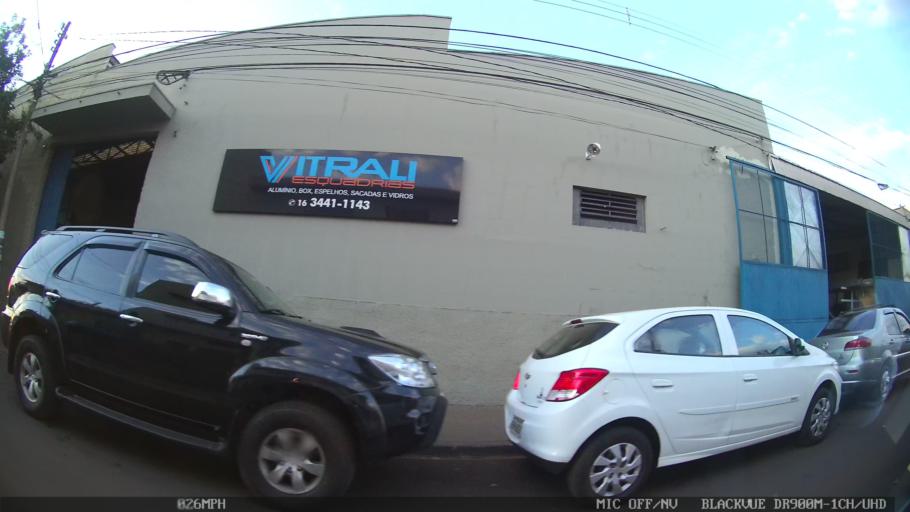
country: BR
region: Sao Paulo
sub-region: Ribeirao Preto
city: Ribeirao Preto
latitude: -21.1485
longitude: -47.7883
